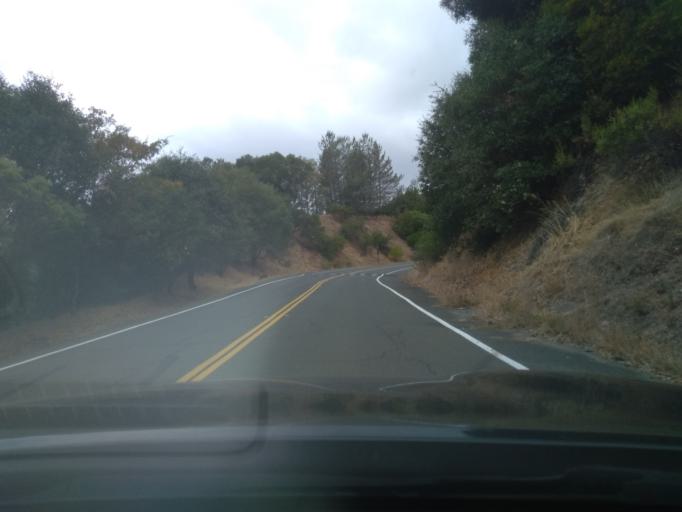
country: US
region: California
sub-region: Mendocino County
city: Ukiah
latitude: 39.2012
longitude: -123.1876
